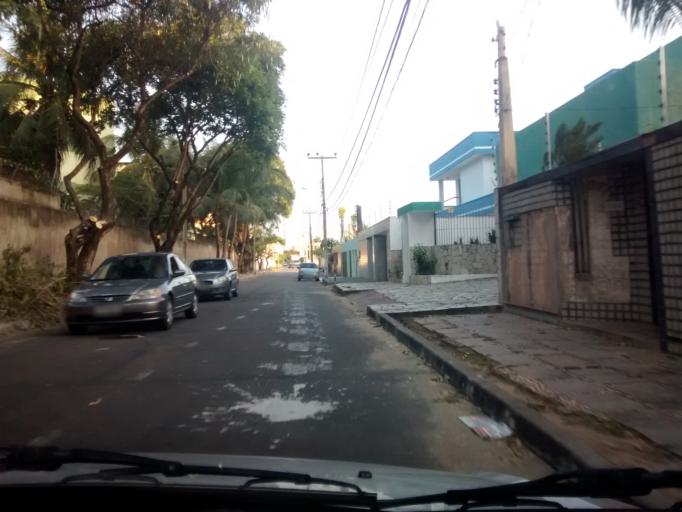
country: BR
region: Rio Grande do Norte
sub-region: Natal
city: Natal
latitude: -5.8654
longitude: -35.1899
